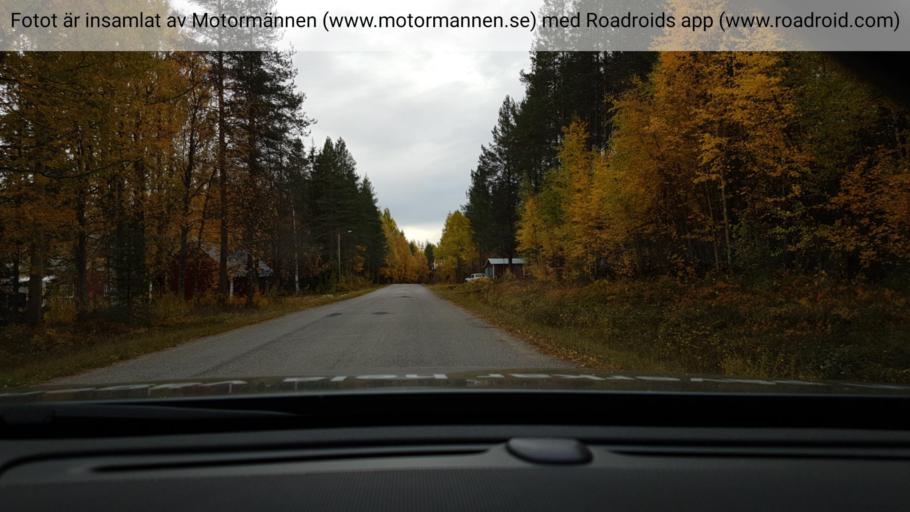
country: SE
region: Norrbotten
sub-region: Overkalix Kommun
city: OEverkalix
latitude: 66.2351
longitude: 23.0089
